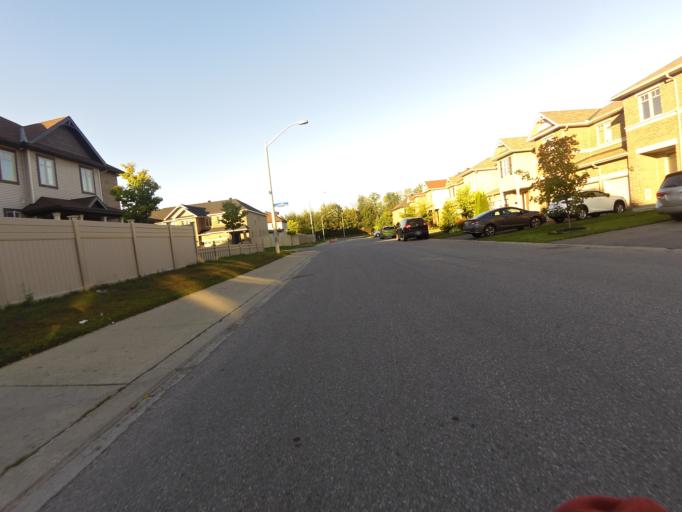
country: CA
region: Ontario
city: Bells Corners
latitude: 45.3621
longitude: -75.9288
